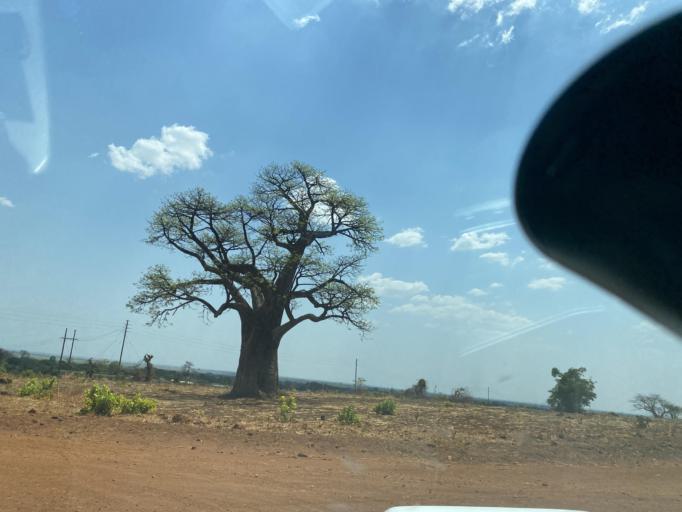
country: ZM
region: Southern
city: Nakambala
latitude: -15.5032
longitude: 27.9286
